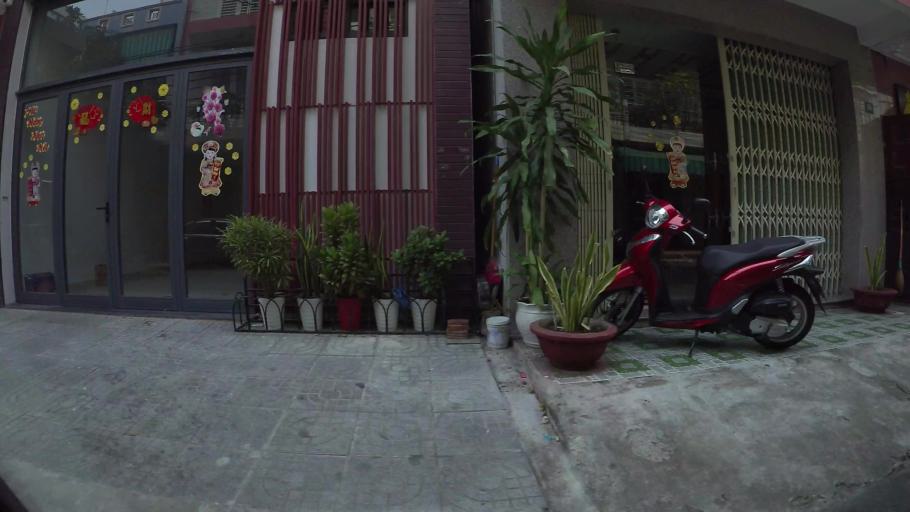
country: VN
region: Da Nang
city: Son Tra
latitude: 16.0371
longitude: 108.2231
